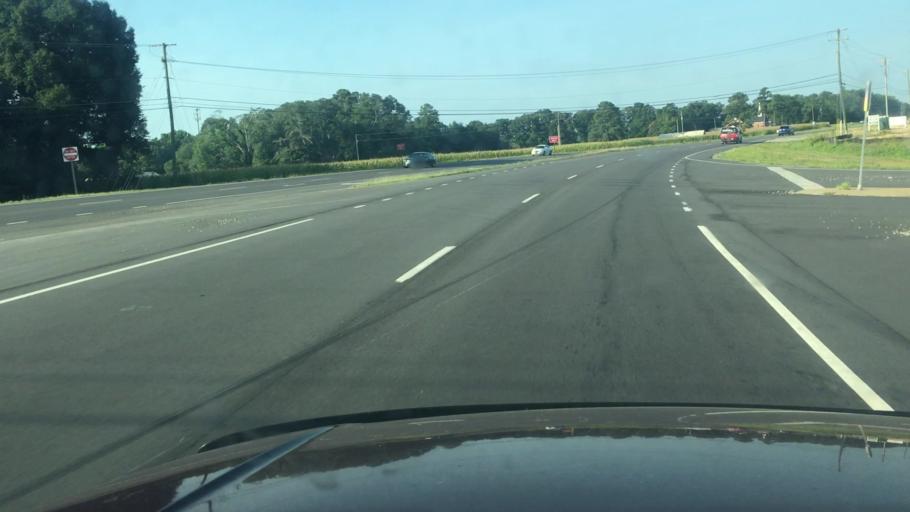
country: US
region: North Carolina
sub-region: Cumberland County
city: Hope Mills
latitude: 34.9363
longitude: -78.8478
